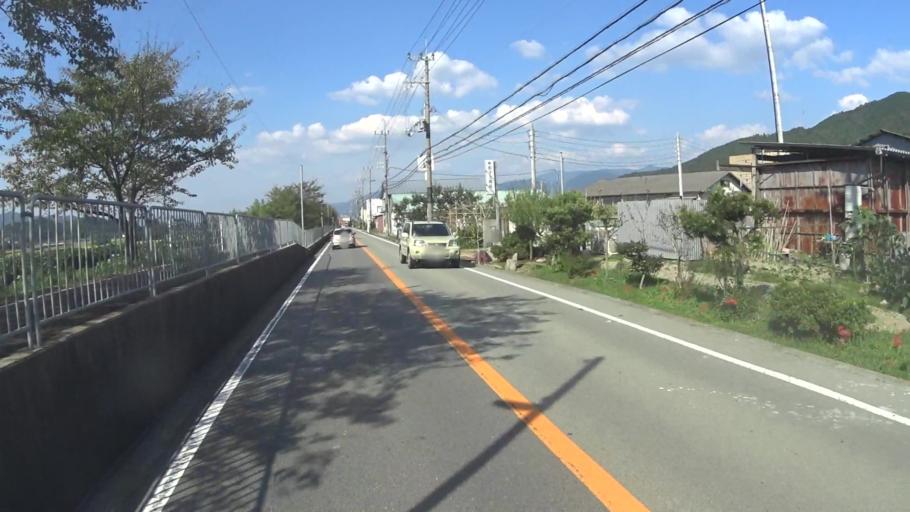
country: JP
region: Kyoto
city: Kameoka
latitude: 34.9923
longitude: 135.5474
